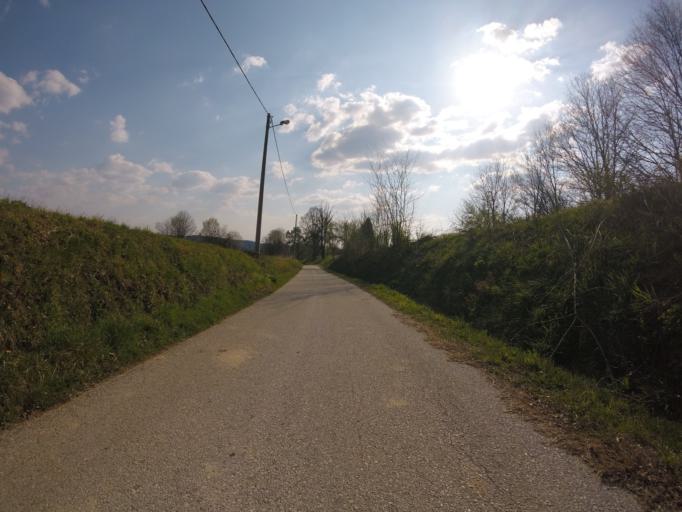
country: HR
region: Sisacko-Moslavacka
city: Glina
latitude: 45.4959
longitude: 16.0035
